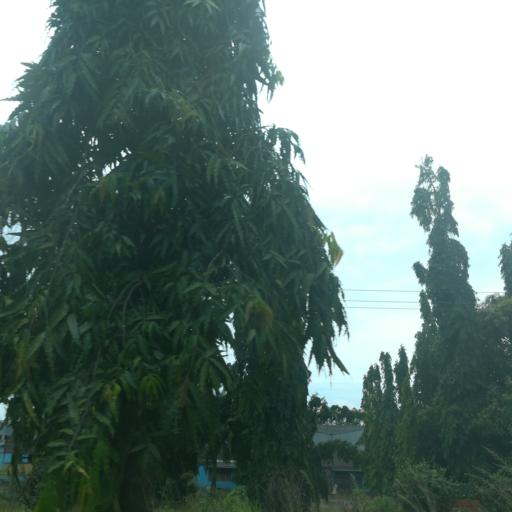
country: NG
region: Lagos
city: Ejirin
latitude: 6.6520
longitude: 3.7128
